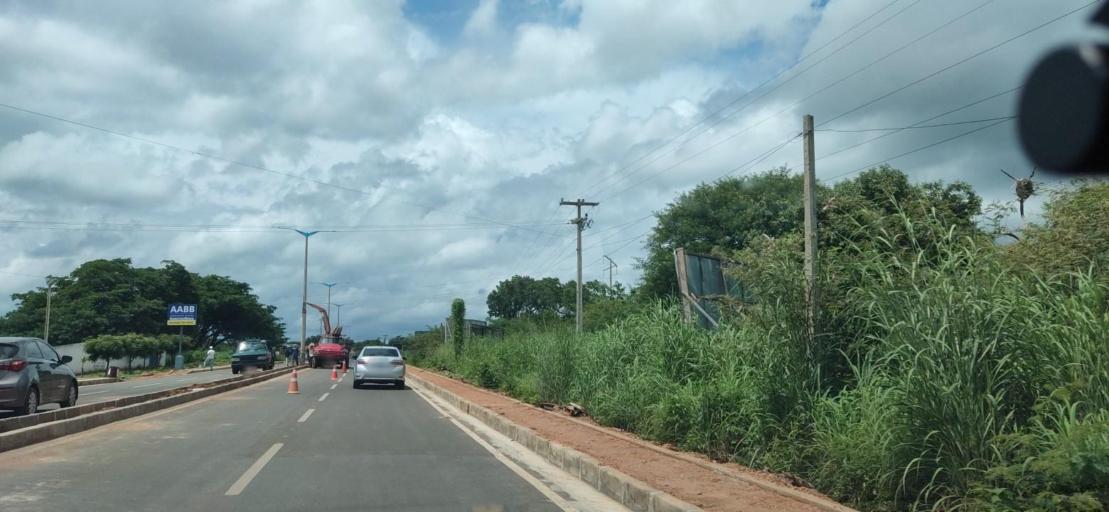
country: BR
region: Piaui
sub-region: Valenca Do Piaui
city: Valenca do Piaui
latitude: -6.4298
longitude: -41.7496
